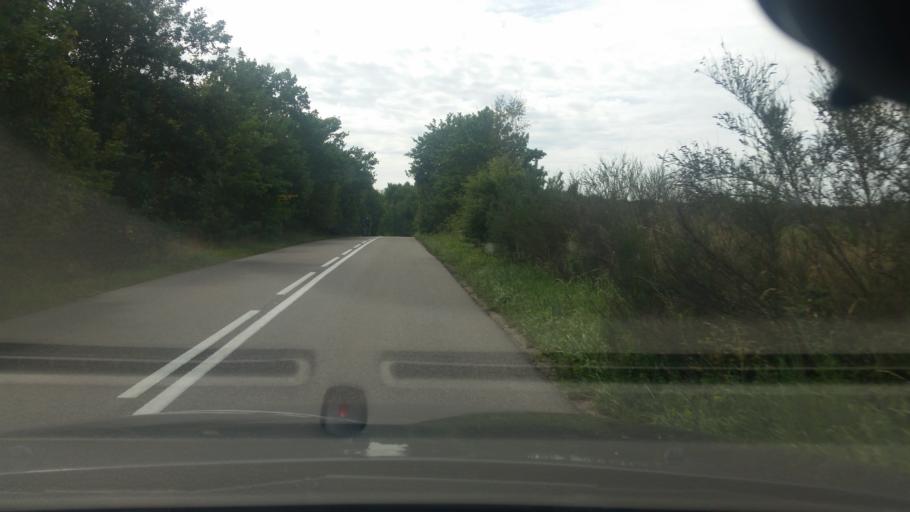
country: PL
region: Pomeranian Voivodeship
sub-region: Powiat leborski
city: Leba
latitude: 54.7483
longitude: 17.6638
